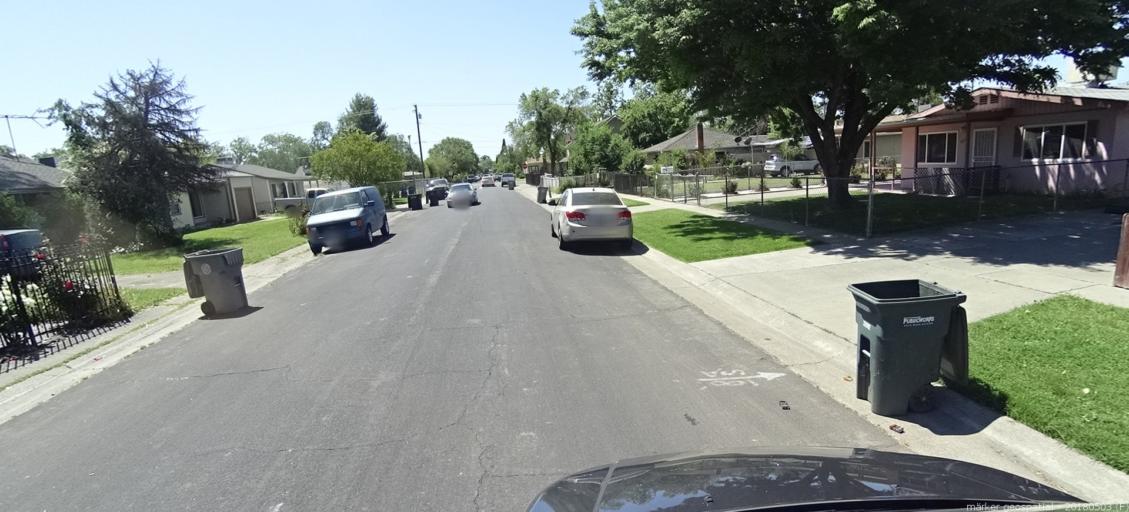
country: US
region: California
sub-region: Sacramento County
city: Rio Linda
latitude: 38.6374
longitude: -121.4278
